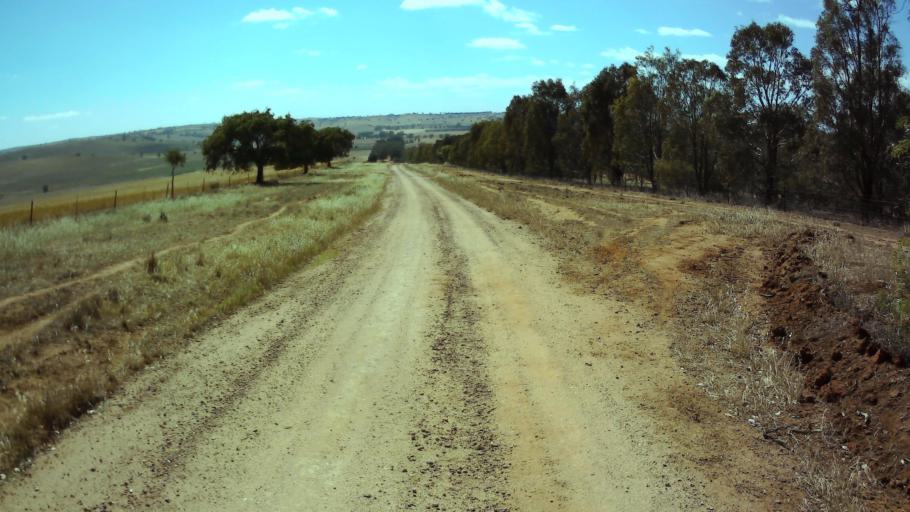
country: AU
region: New South Wales
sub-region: Weddin
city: Grenfell
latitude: -33.9533
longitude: 148.4007
